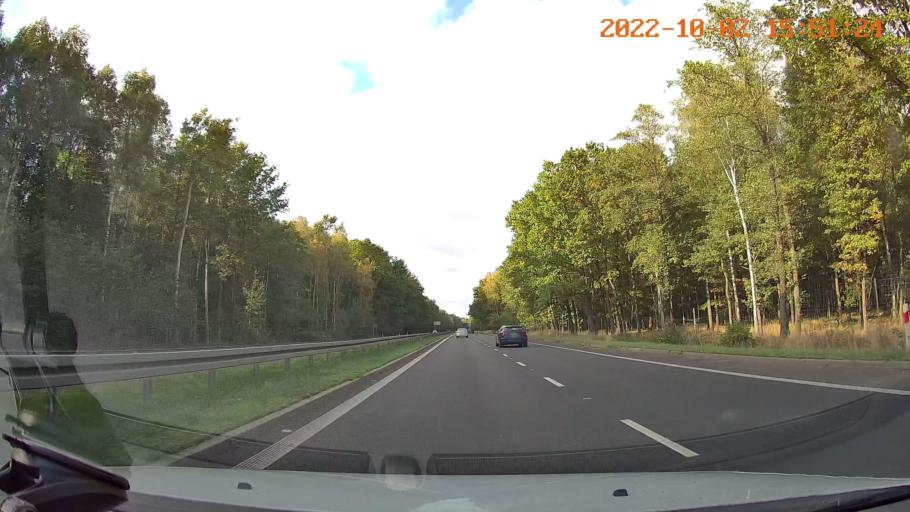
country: PL
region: Silesian Voivodeship
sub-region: Tychy
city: Cielmice
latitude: 50.1400
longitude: 19.0251
